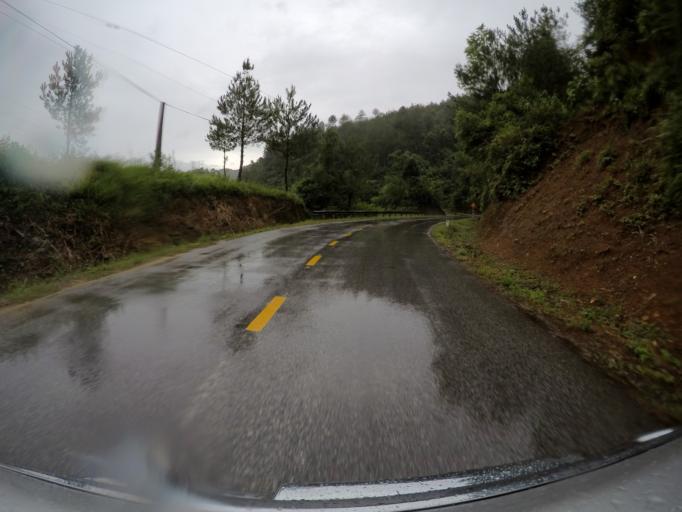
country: VN
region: Lai Chau
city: Than Uyen
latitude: 22.0662
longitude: 103.8646
